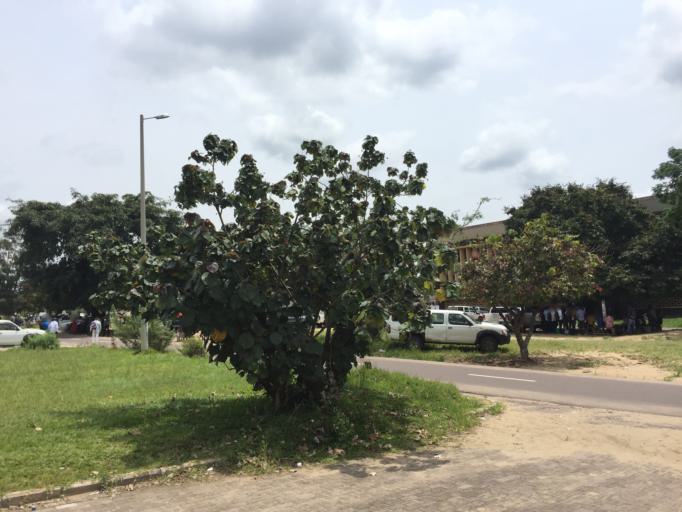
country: CD
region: Kinshasa
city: Masina
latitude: -4.4184
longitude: 15.3085
